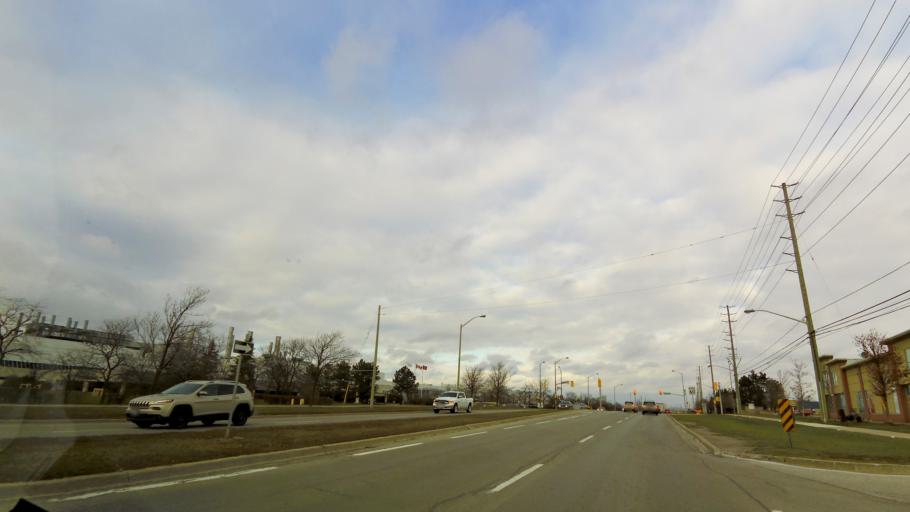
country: CA
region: Ontario
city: Brampton
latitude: 43.7477
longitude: -79.7159
